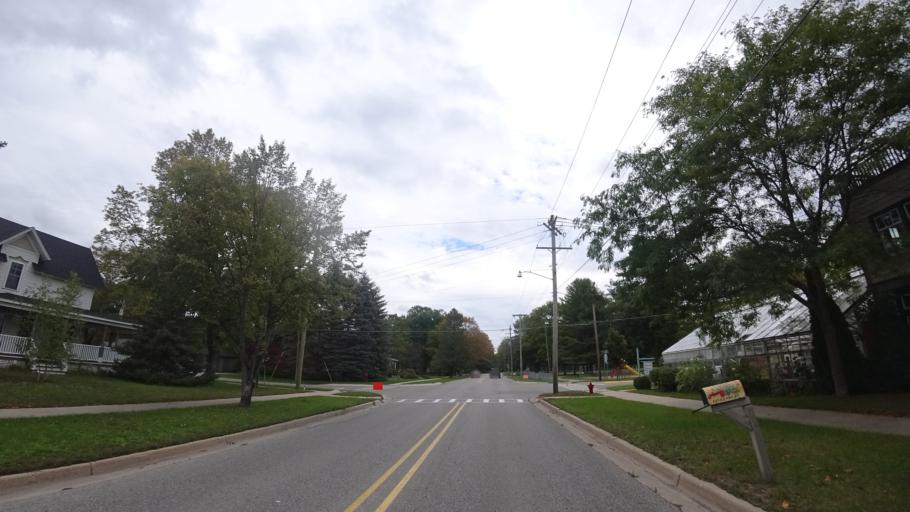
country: US
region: Michigan
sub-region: Emmet County
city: Harbor Springs
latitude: 45.4354
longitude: -84.9756
